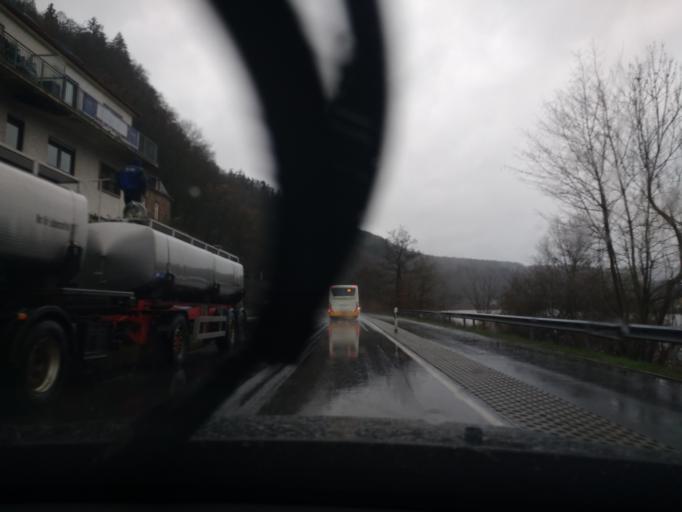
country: DE
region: Rheinland-Pfalz
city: Traben-Trarbach
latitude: 49.9509
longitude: 7.1084
